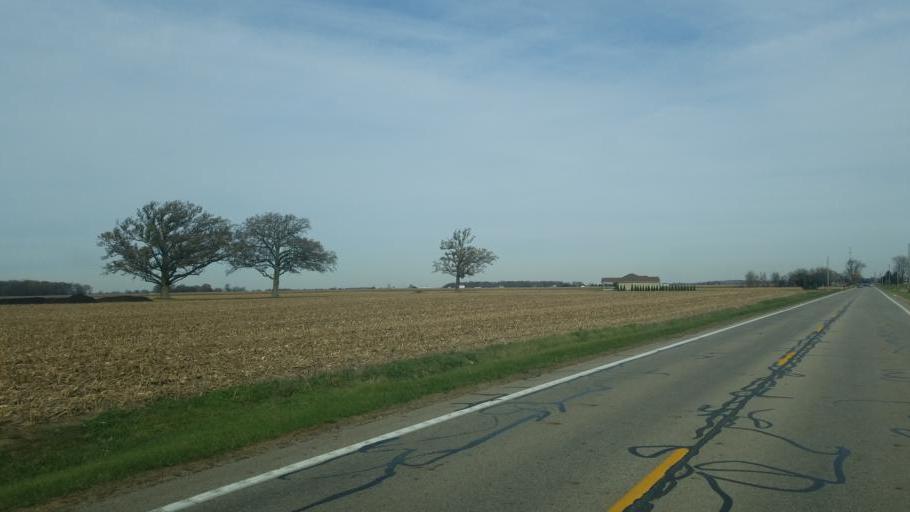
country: US
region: Ohio
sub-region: Madison County
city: West Jefferson
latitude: 40.0036
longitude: -83.3193
